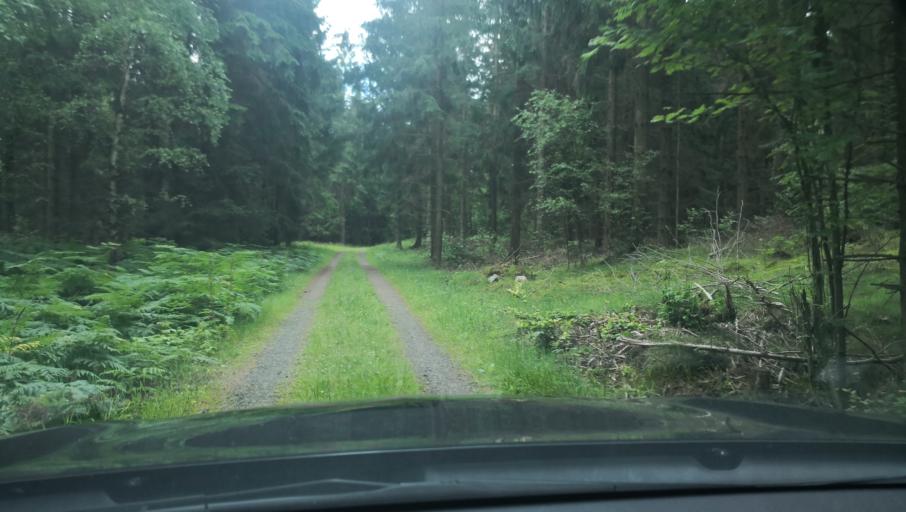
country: SE
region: Skane
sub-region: Simrishamns Kommun
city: Kivik
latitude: 55.6124
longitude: 14.1182
